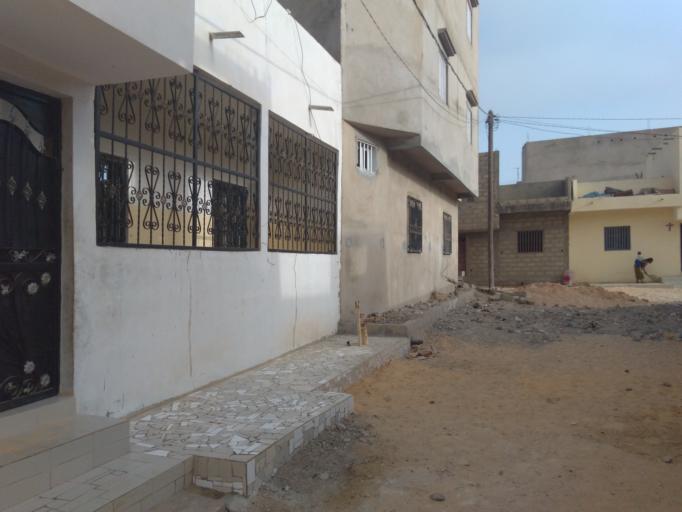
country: SN
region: Dakar
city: Pikine
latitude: 14.8000
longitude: -17.3399
